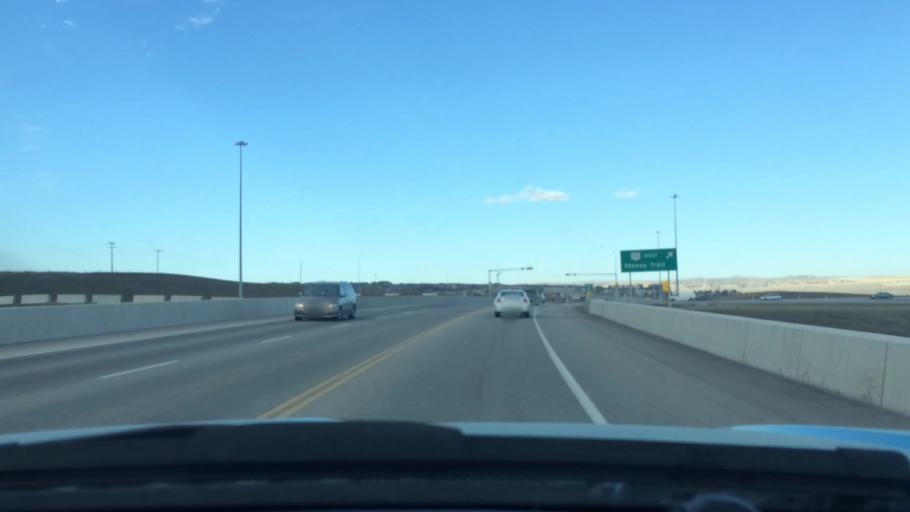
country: CA
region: Alberta
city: Calgary
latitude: 51.1525
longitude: -114.1405
